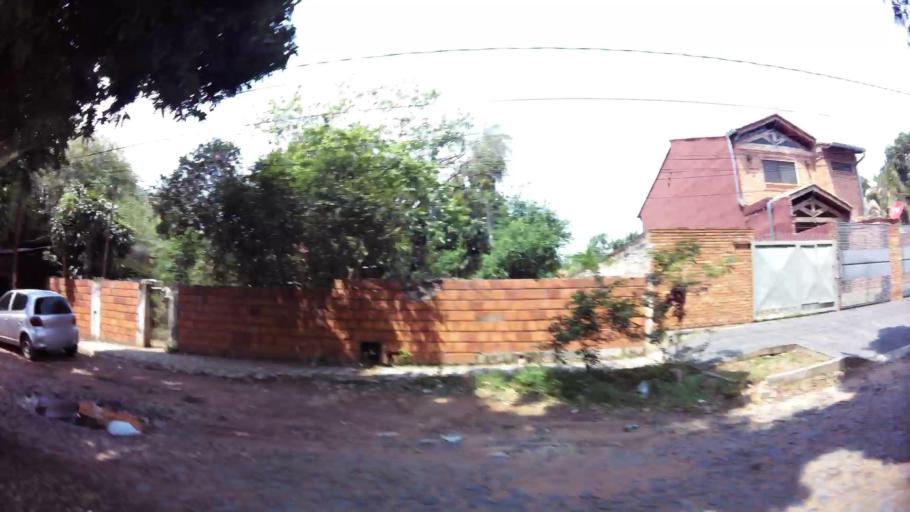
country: PY
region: Asuncion
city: Asuncion
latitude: -25.2828
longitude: -57.6086
